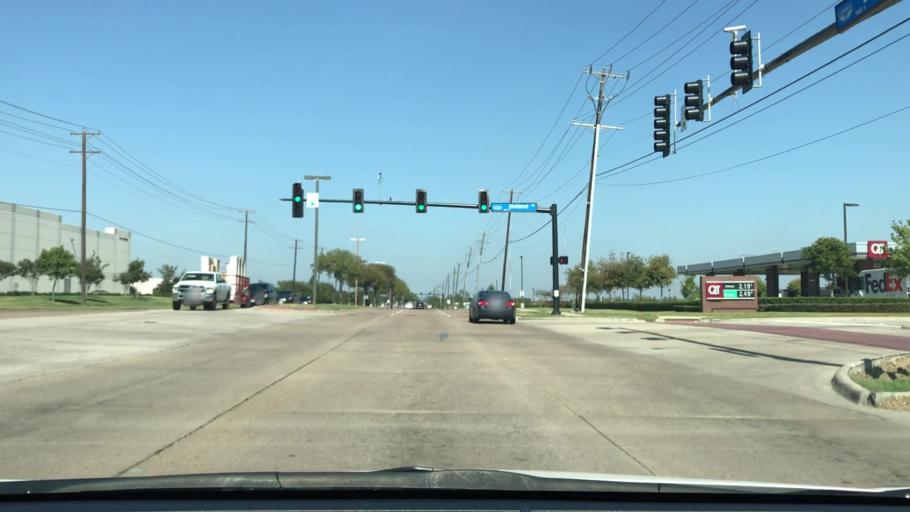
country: US
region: Texas
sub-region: Dallas County
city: Coppell
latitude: 32.9298
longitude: -96.9935
